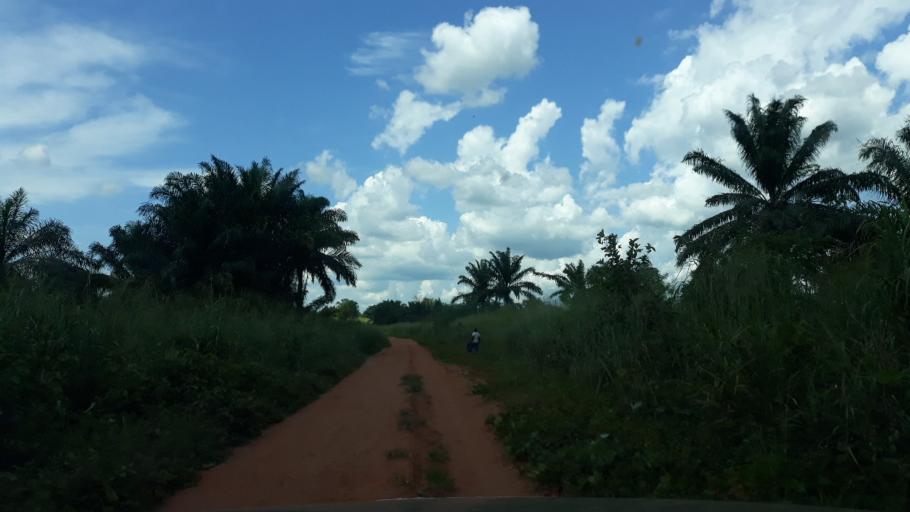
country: CD
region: Equateur
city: Businga
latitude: 3.4040
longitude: 20.3853
